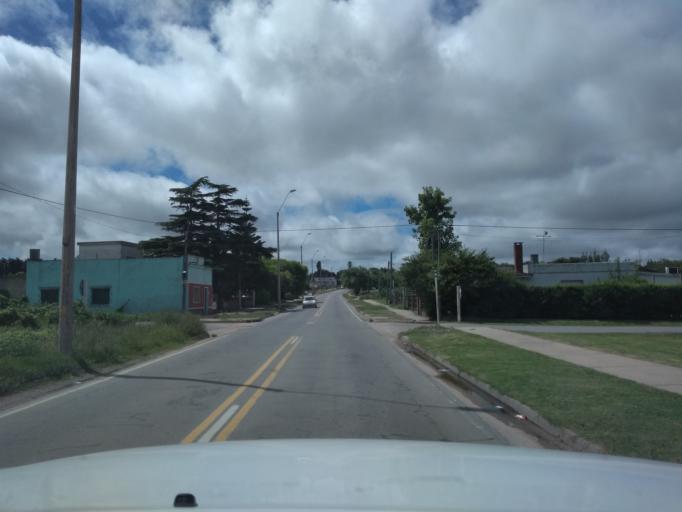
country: UY
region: Canelones
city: Pando
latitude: -34.7138
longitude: -55.9631
